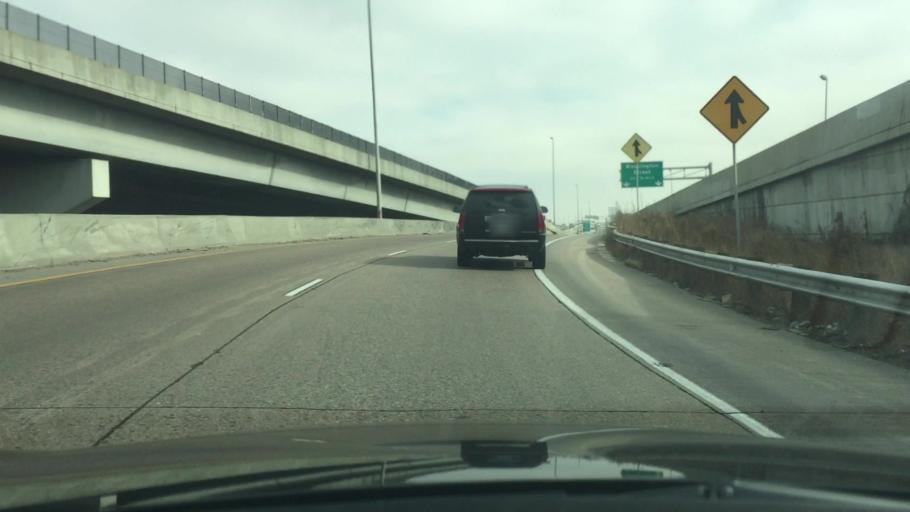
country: US
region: Colorado
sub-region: Denver County
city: Denver
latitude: 39.7795
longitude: -104.9873
